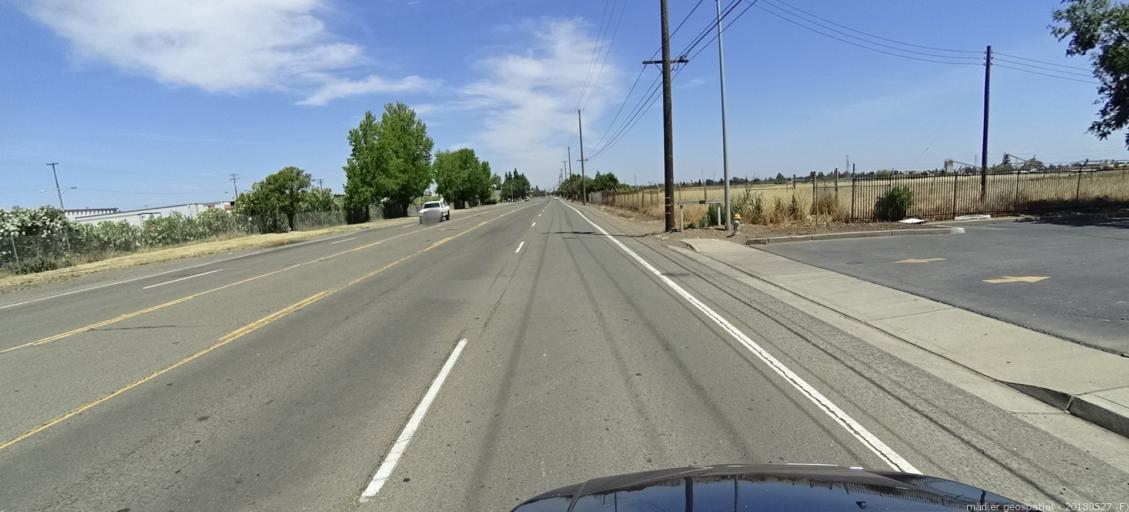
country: US
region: California
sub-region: Sacramento County
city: Rosemont
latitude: 38.5344
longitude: -121.3907
